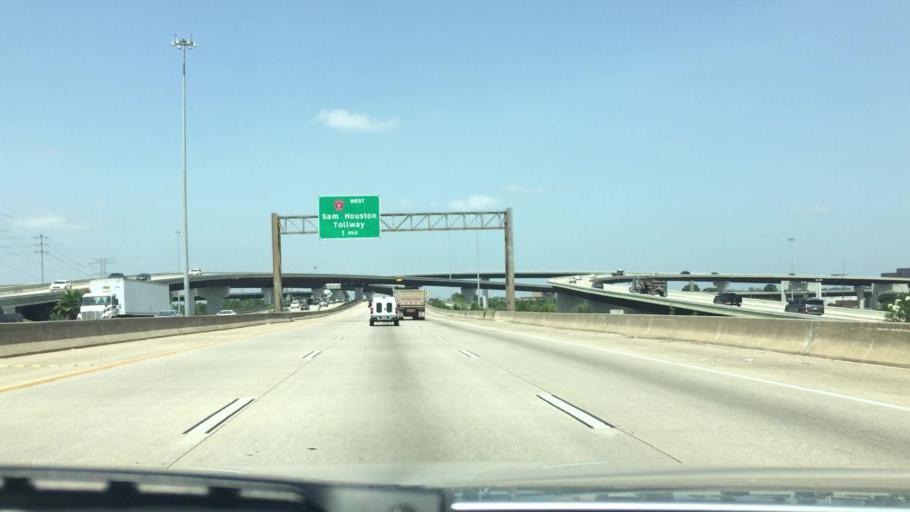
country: US
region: Texas
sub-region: Harris County
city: Aldine
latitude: 29.9408
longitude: -95.4095
